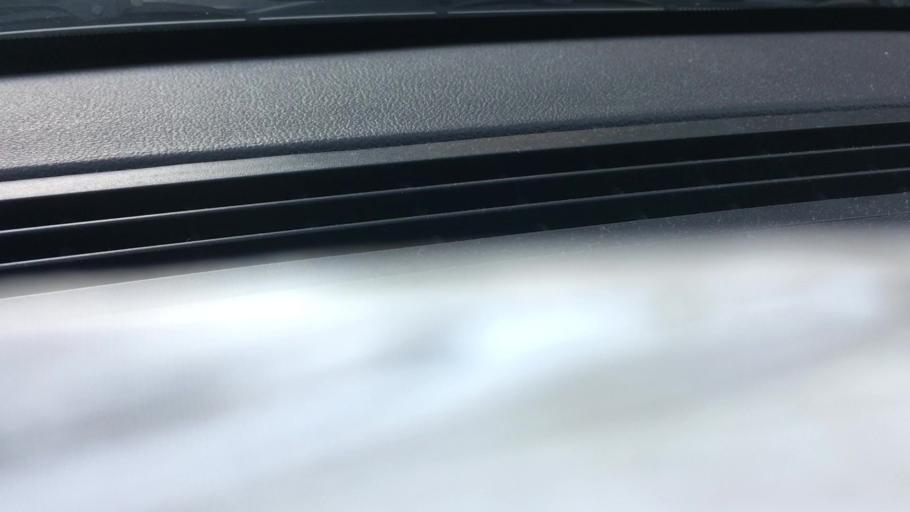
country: US
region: Alabama
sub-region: Shelby County
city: Helena
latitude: 33.2320
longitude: -86.9725
